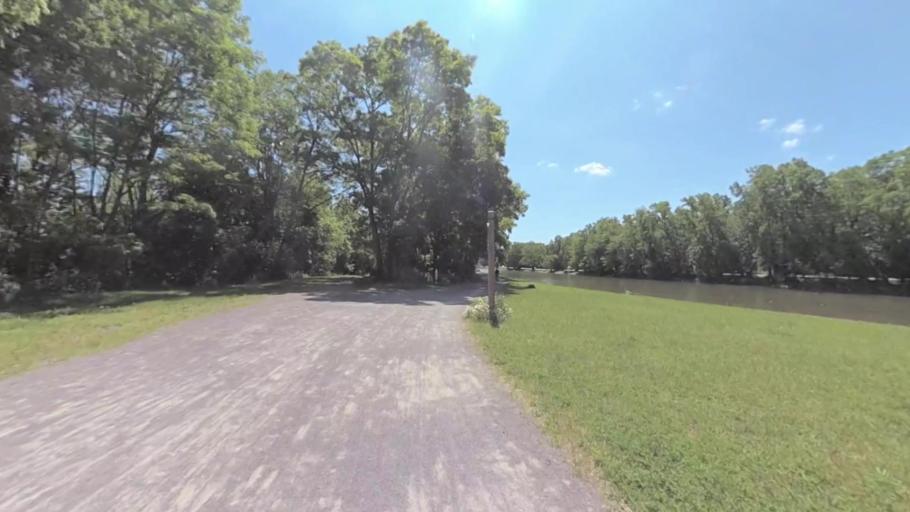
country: US
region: New York
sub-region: Monroe County
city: Pittsford
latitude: 43.0781
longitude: -77.4989
